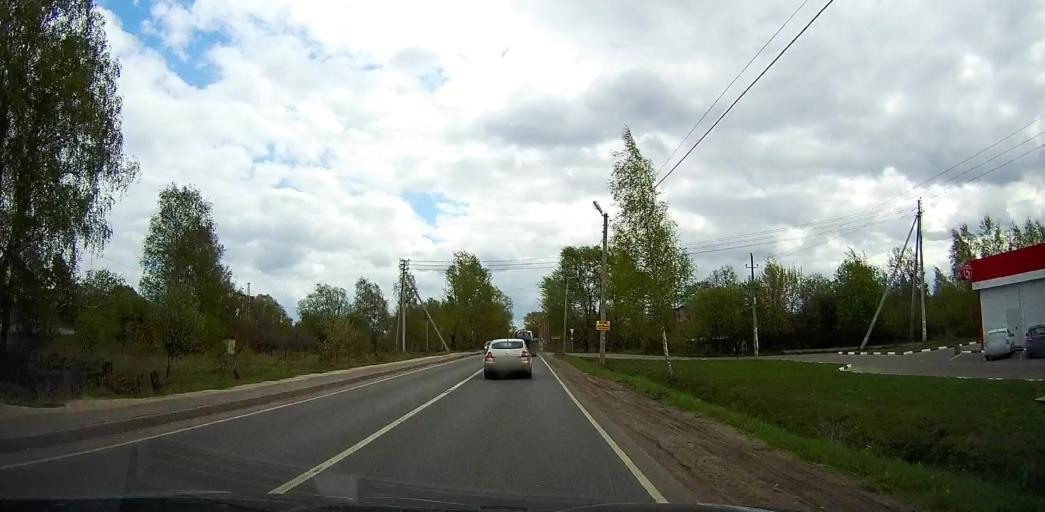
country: RU
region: Moskovskaya
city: Beloozerskiy
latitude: 55.4462
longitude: 38.4913
